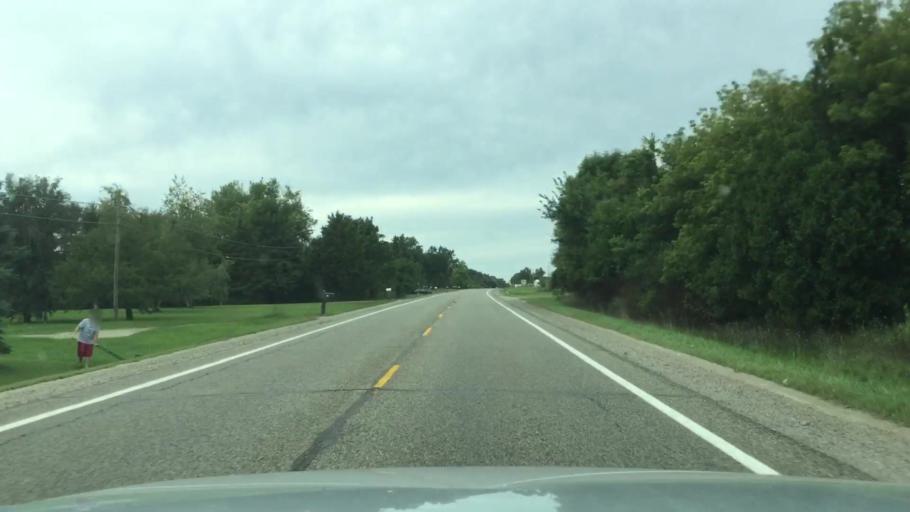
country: US
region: Michigan
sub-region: Shiawassee County
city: Durand
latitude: 42.9351
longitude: -84.0141
